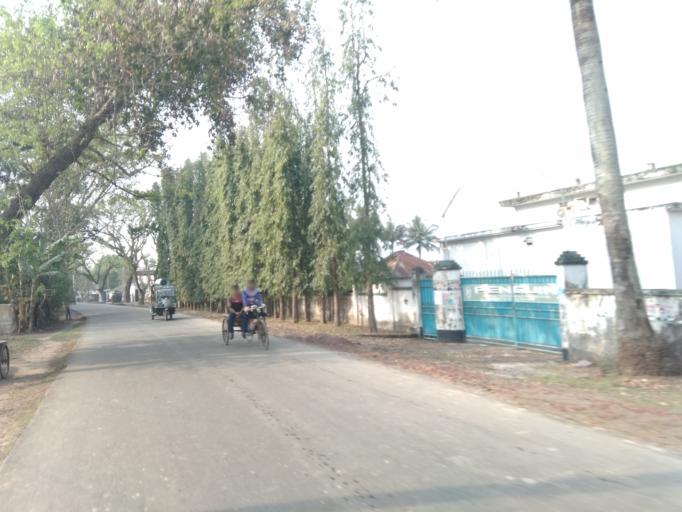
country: IN
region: West Bengal
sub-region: North 24 Parganas
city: Taki
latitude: 22.3277
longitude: 89.1054
